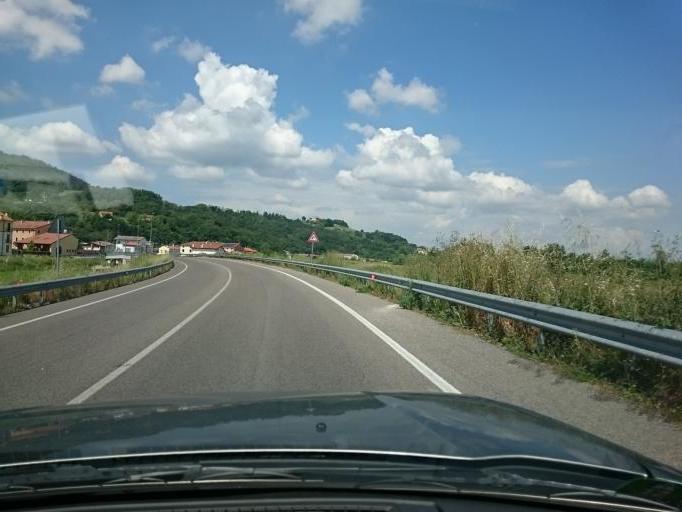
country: IT
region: Veneto
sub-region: Provincia di Vicenza
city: Longare
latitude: 45.4806
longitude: 11.6087
